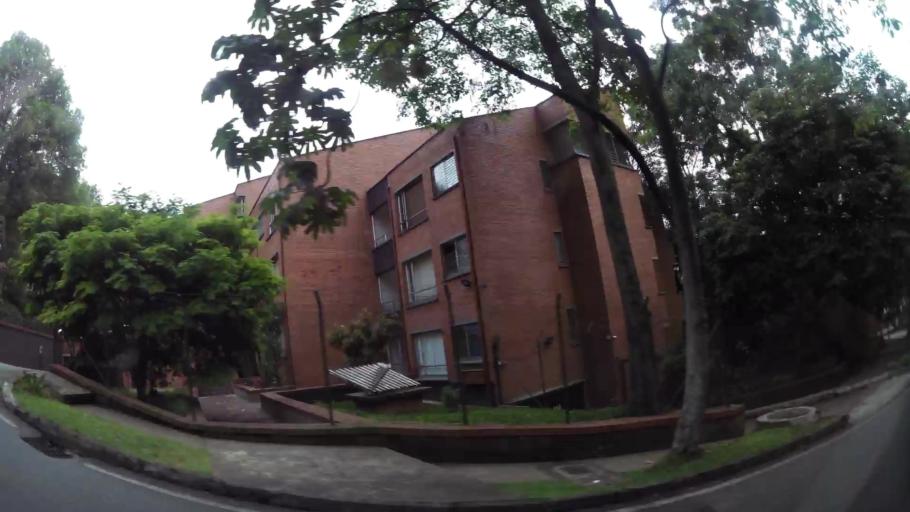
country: CO
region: Antioquia
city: Envigado
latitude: 6.1815
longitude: -75.5716
